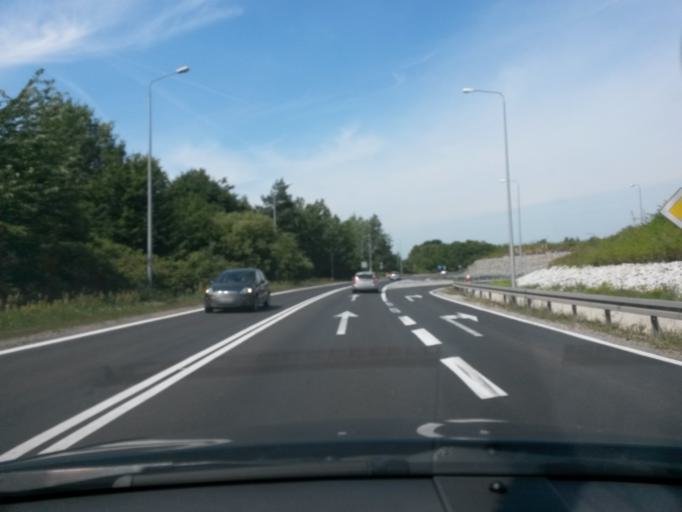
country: PL
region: Lower Silesian Voivodeship
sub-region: Powiat legnicki
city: Prochowice
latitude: 51.2719
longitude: 16.3532
